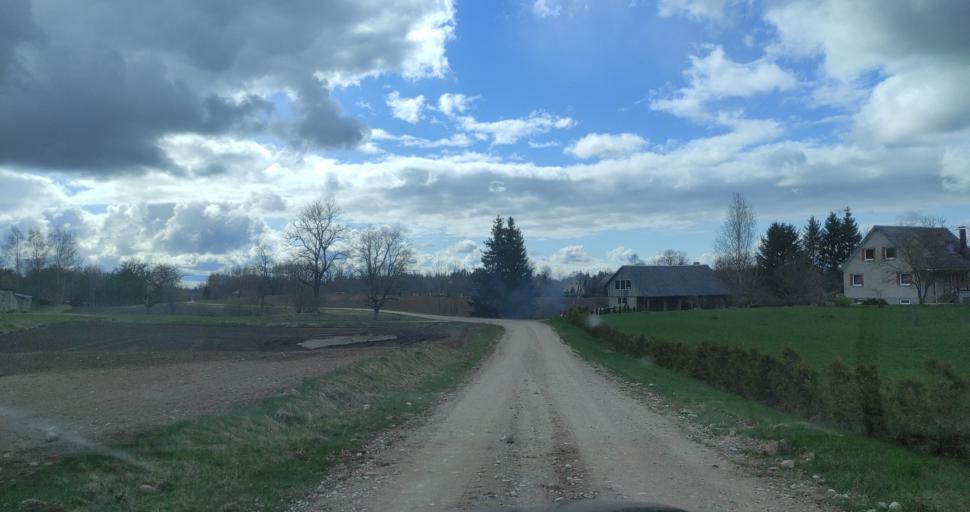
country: LV
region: Aizpute
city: Aizpute
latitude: 56.7125
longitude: 21.5763
